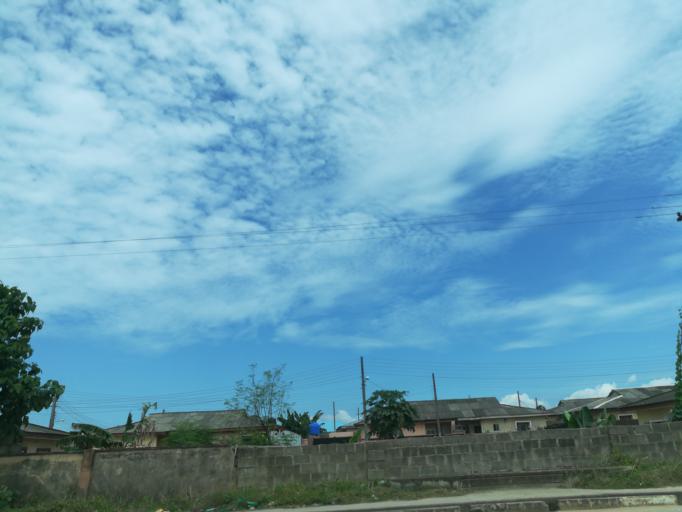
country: NG
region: Lagos
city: Ebute Ikorodu
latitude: 6.5554
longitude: 3.4759
